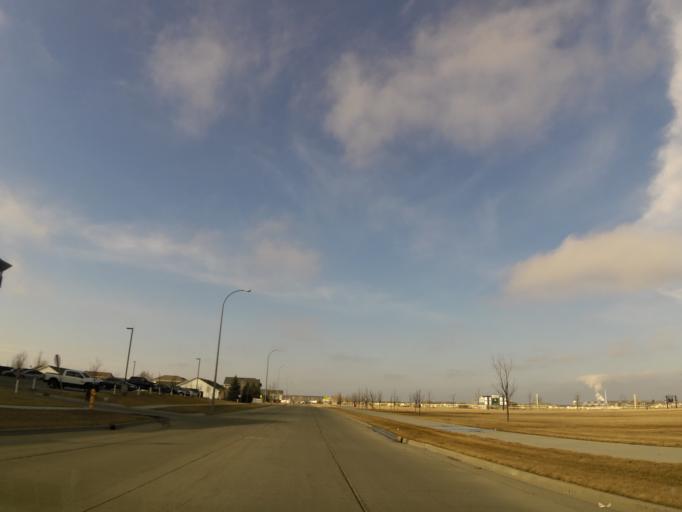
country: US
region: North Dakota
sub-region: Grand Forks County
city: Grand Forks
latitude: 47.8755
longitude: -97.0577
